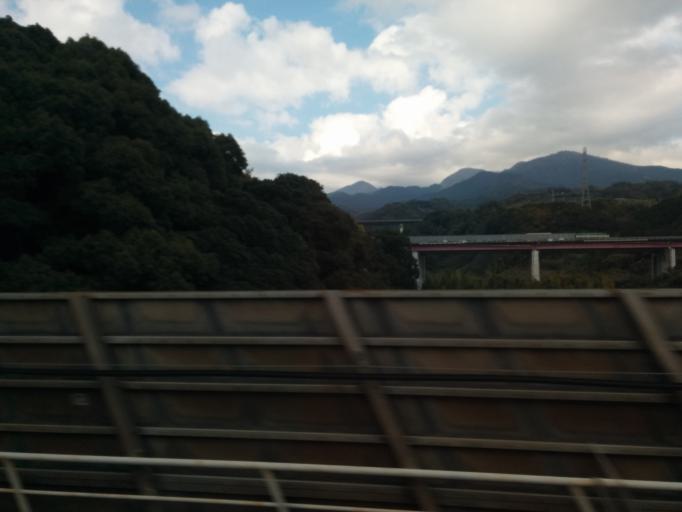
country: JP
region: Shizuoka
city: Fuji
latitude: 35.1517
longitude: 138.7756
